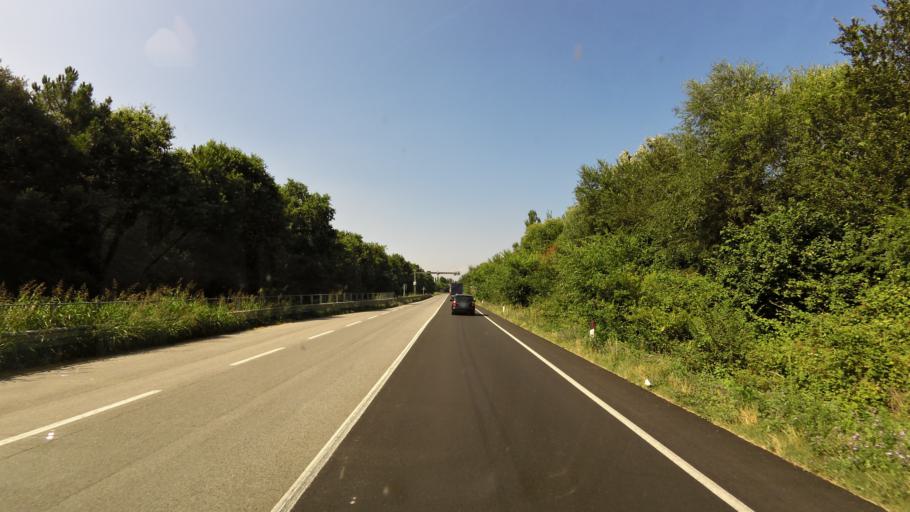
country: IT
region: Emilia-Romagna
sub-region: Provincia di Ravenna
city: Ravenna
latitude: 44.4702
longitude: 12.2092
